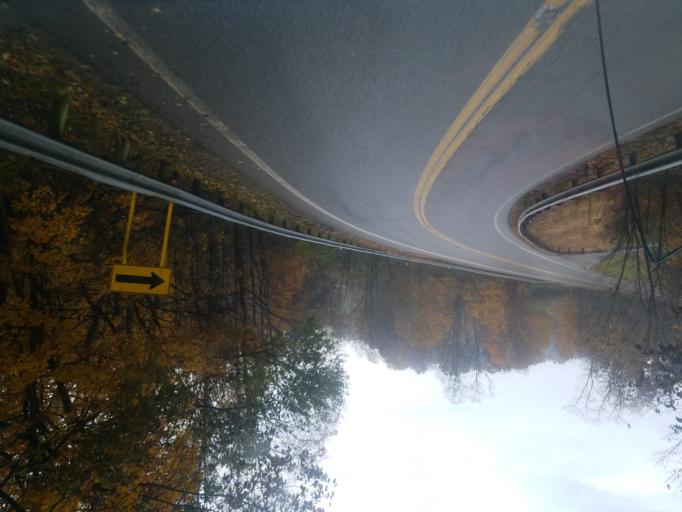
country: US
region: Ohio
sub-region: Morgan County
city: McConnelsville
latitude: 39.4781
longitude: -81.8720
